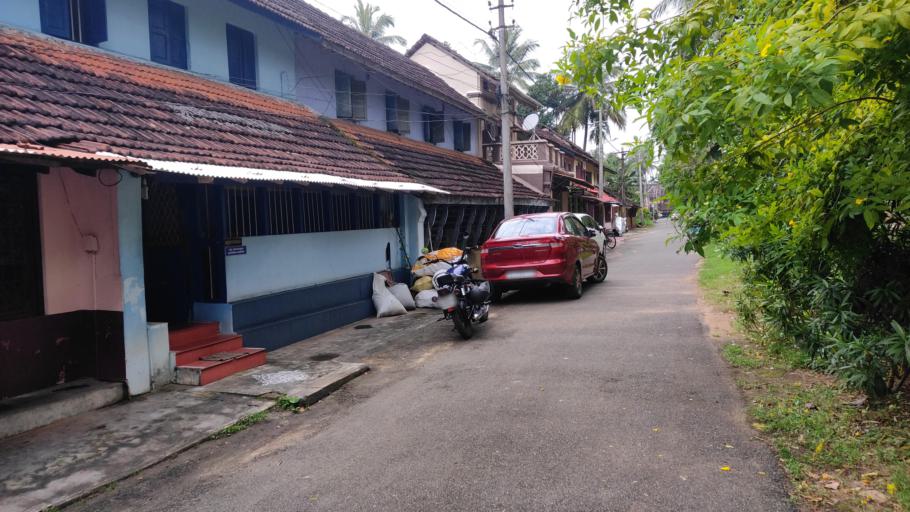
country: IN
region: Kerala
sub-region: Palakkad district
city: Chittur
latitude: 10.6921
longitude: 76.7415
